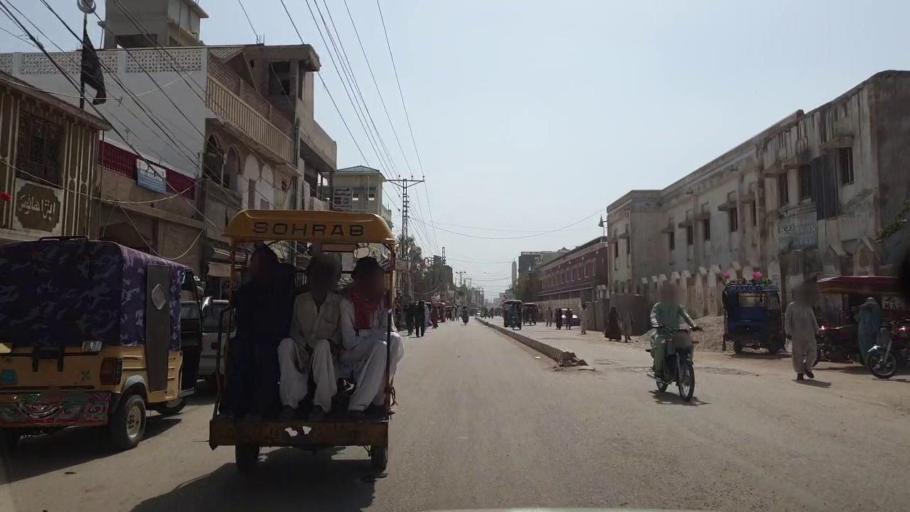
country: PK
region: Sindh
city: Matli
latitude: 25.0450
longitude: 68.6561
